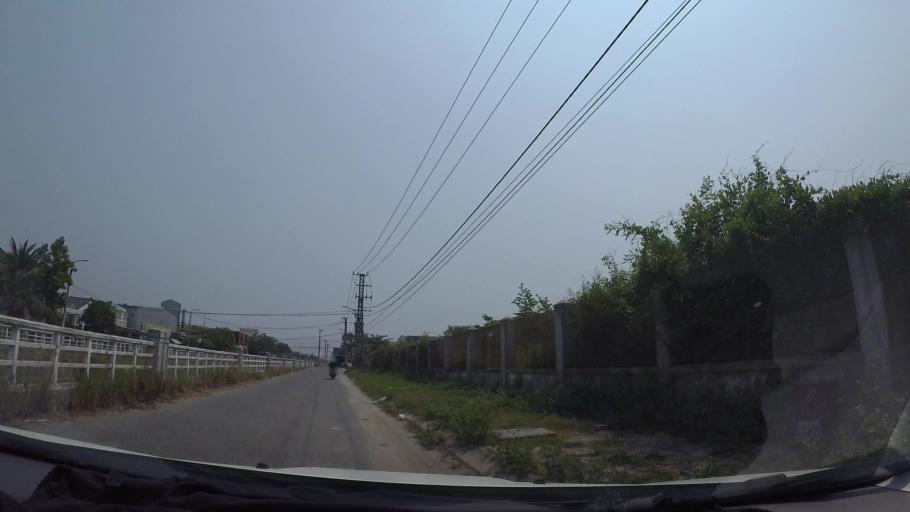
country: VN
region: Da Nang
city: Cam Le
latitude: 15.9825
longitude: 108.2071
